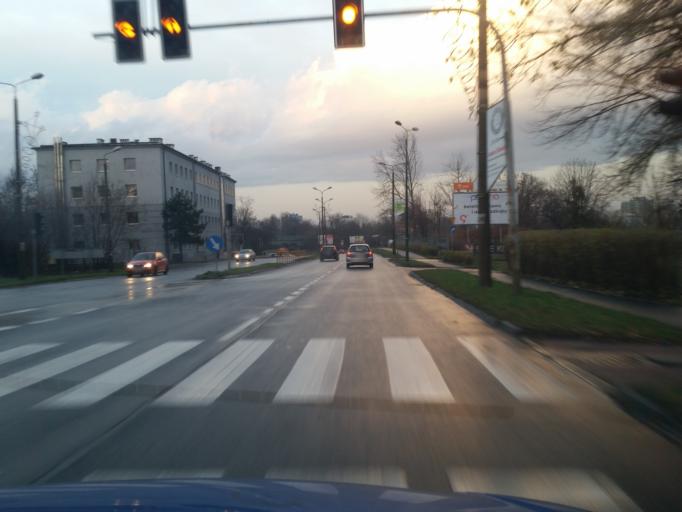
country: PL
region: Silesian Voivodeship
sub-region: Dabrowa Gornicza
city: Dabrowa Gornicza
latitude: 50.3140
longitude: 19.1956
